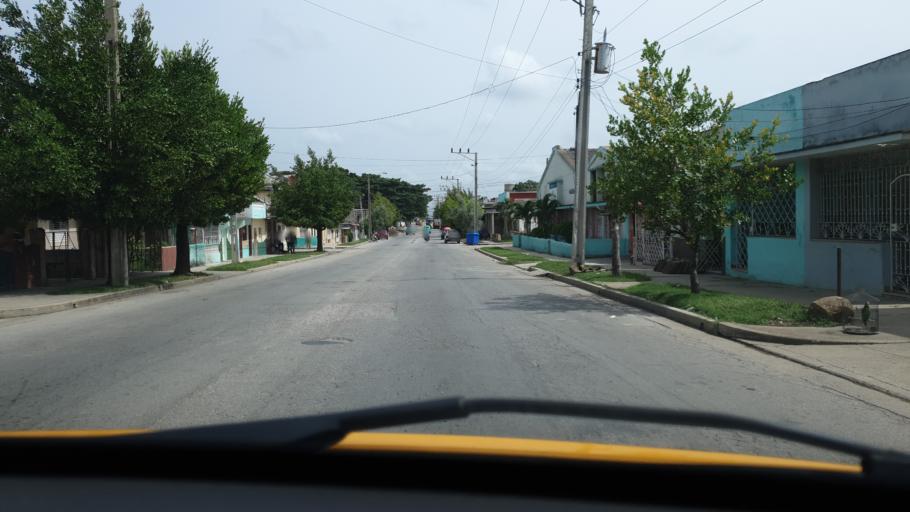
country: CU
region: Villa Clara
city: Santa Clara
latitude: 22.3922
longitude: -79.9609
